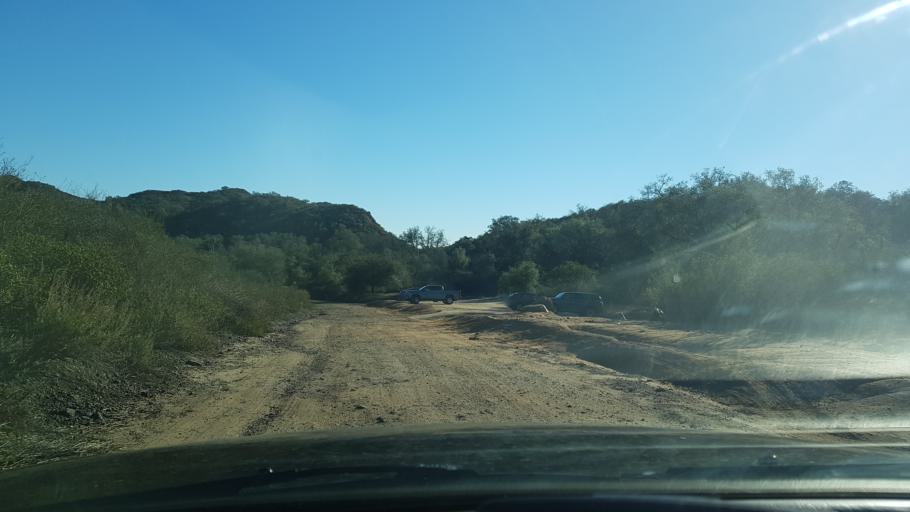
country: US
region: California
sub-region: San Diego County
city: Hidden Meadows
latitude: 33.2104
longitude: -117.0857
